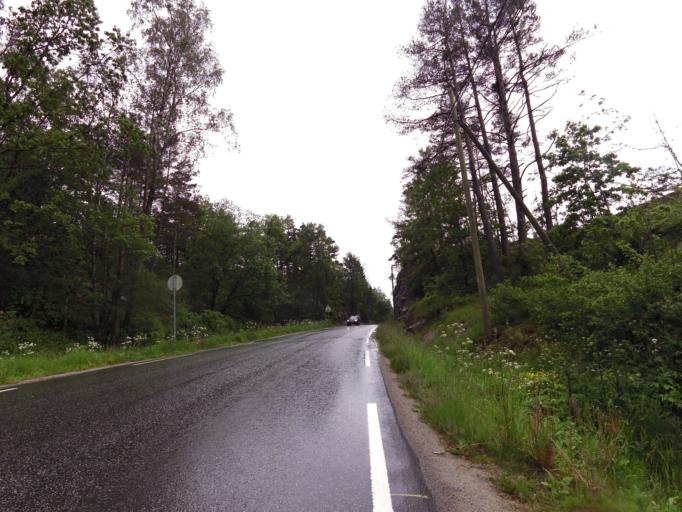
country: NO
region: Vest-Agder
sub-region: Mandal
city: Mandal
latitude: 58.0206
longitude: 7.5161
